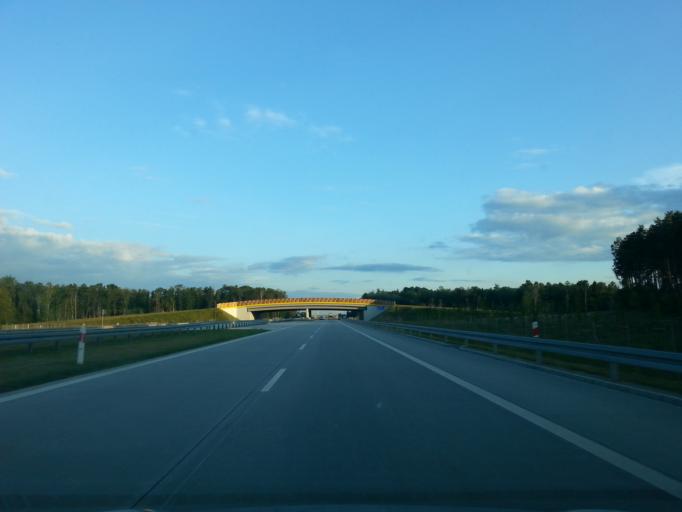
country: PL
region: Lodz Voivodeship
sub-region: Powiat sieradzki
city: Zloczew
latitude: 51.4409
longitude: 18.6458
